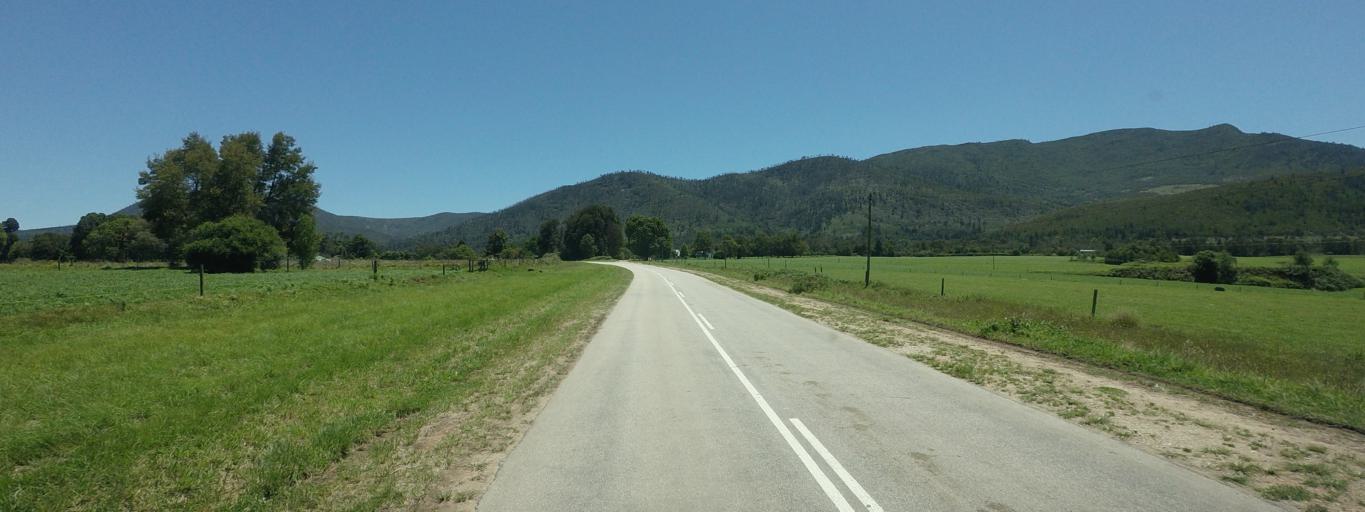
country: ZA
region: Western Cape
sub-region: Eden District Municipality
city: Plettenberg Bay
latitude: -33.9402
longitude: 23.5102
